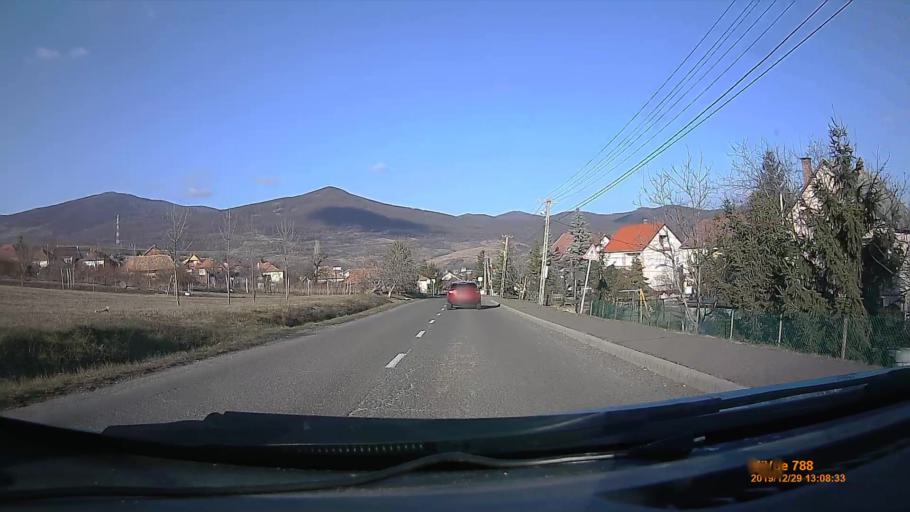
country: HU
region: Heves
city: Abasar
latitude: 47.8181
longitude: 20.0535
